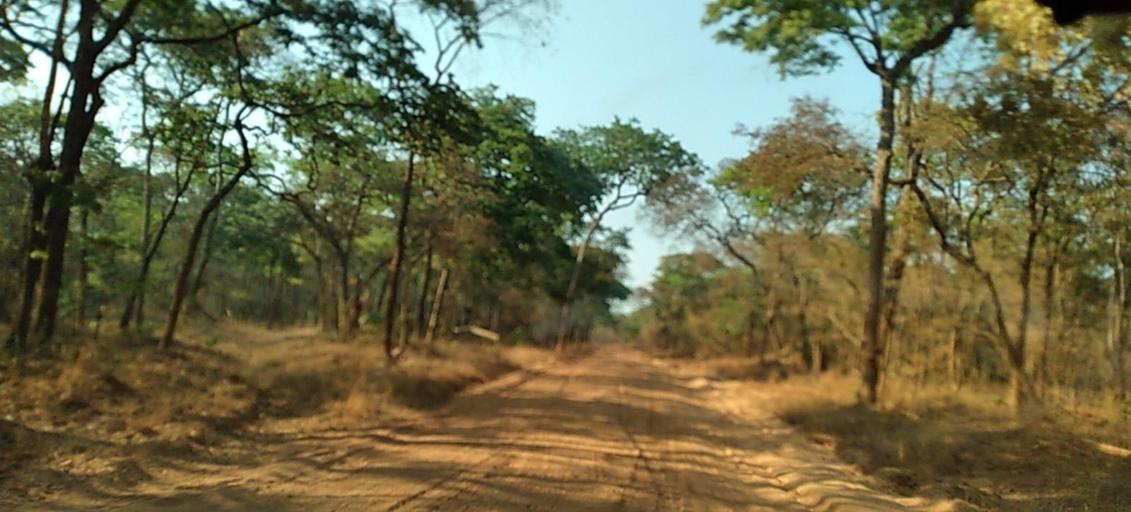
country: ZM
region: North-Western
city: Kasempa
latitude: -13.6133
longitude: 25.9789
